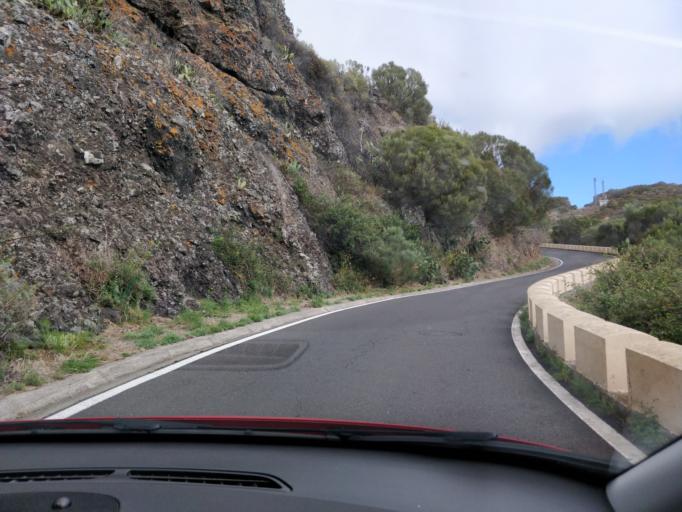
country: ES
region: Canary Islands
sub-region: Provincia de Santa Cruz de Tenerife
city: Santiago del Teide
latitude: 28.3193
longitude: -16.8539
